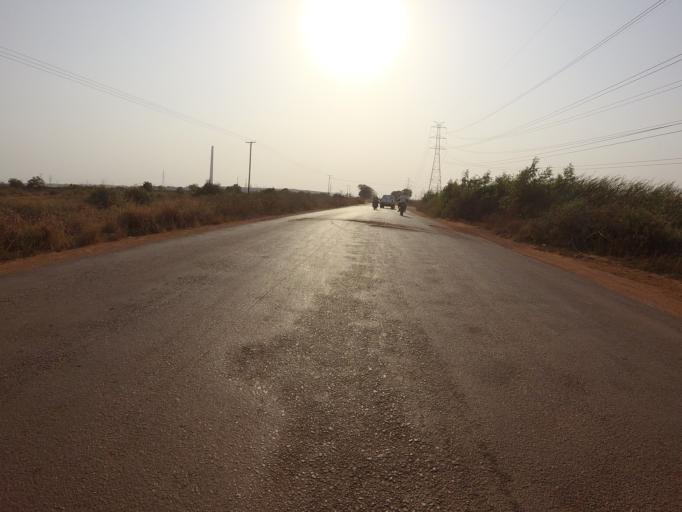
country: GH
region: Greater Accra
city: Tema
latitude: 5.6753
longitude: 0.0307
